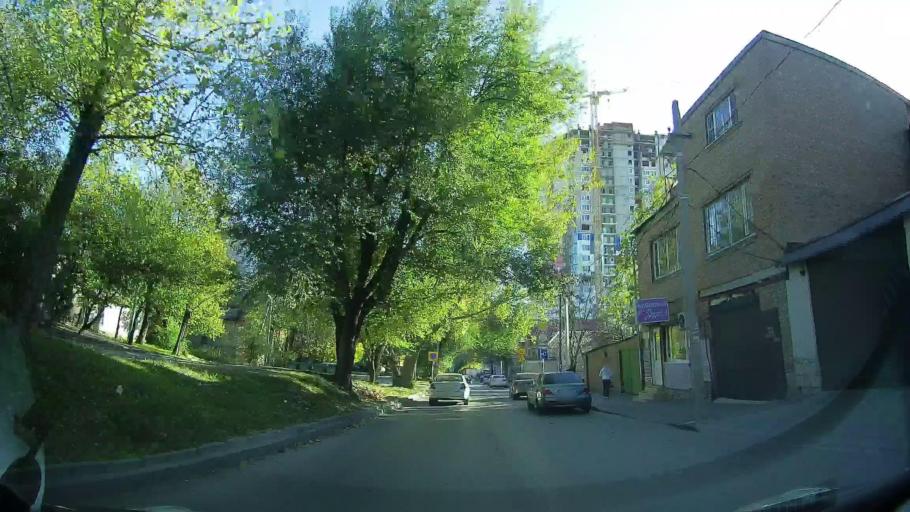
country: RU
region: Rostov
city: Rostov-na-Donu
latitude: 47.2274
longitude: 39.6911
